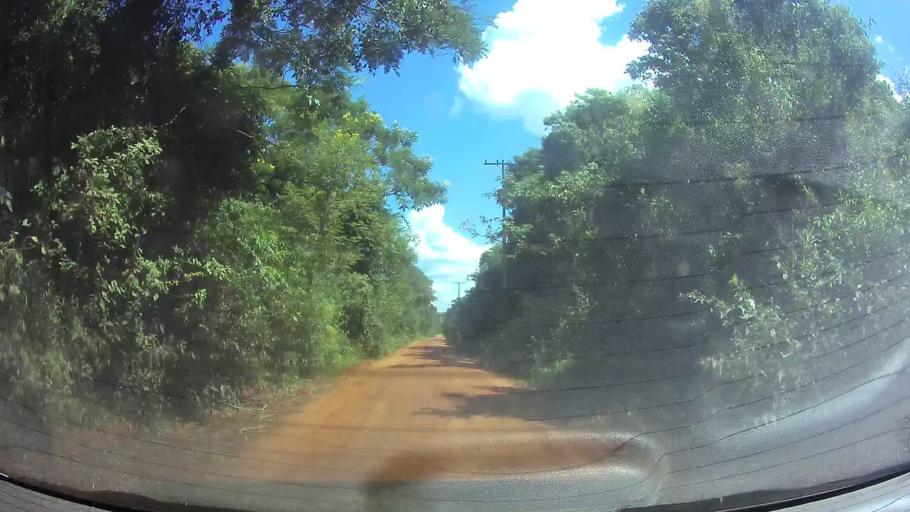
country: PY
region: Paraguari
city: La Colmena
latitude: -25.9470
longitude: -56.7812
